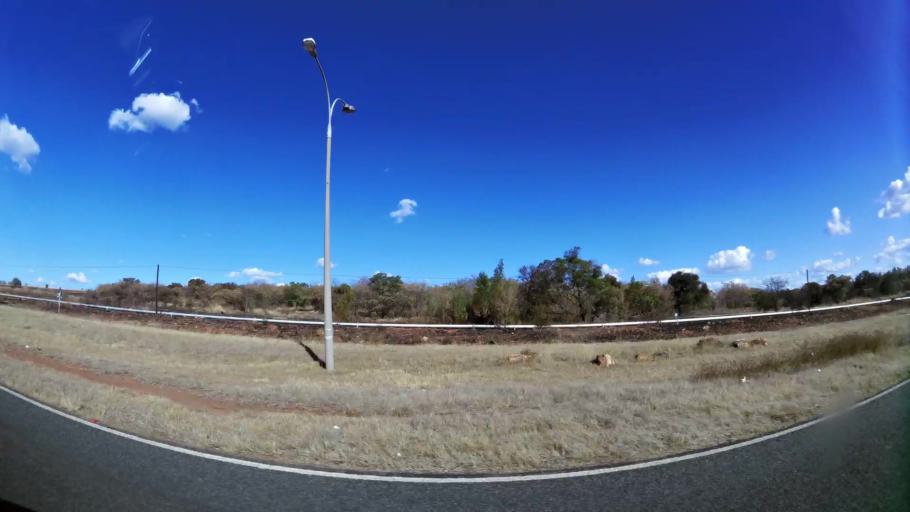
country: ZA
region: Gauteng
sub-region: West Rand District Municipality
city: Carletonville
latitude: -26.3759
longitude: 27.3993
